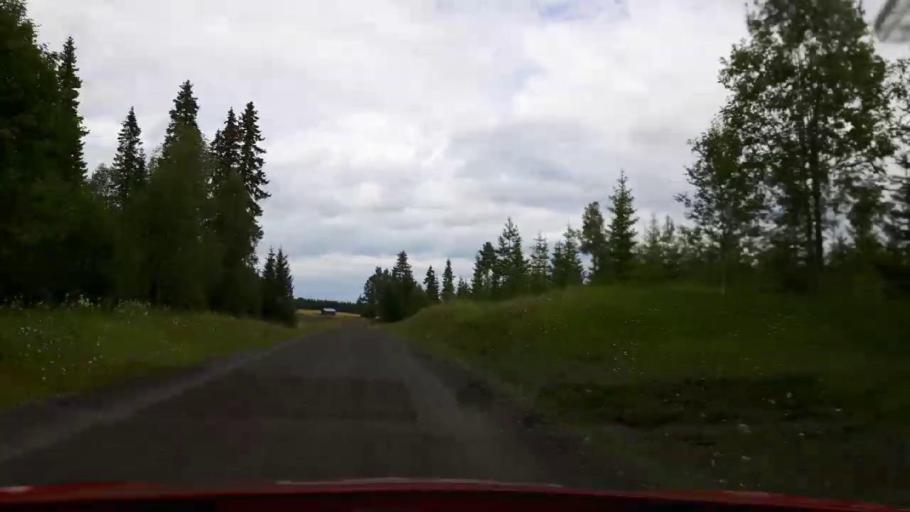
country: SE
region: Jaemtland
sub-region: OEstersunds Kommun
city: Lit
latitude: 63.4375
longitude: 15.2669
